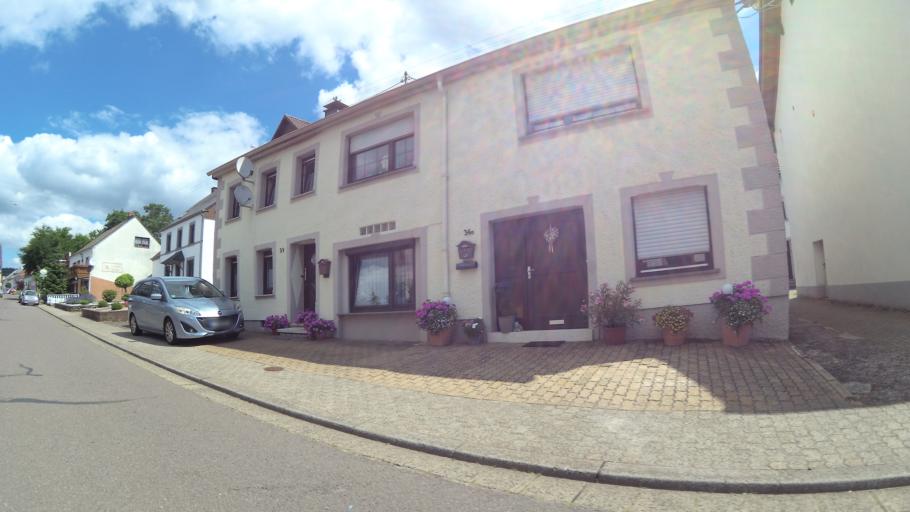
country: DE
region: Saarland
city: Weiskirchen
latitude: 49.5537
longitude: 6.8322
